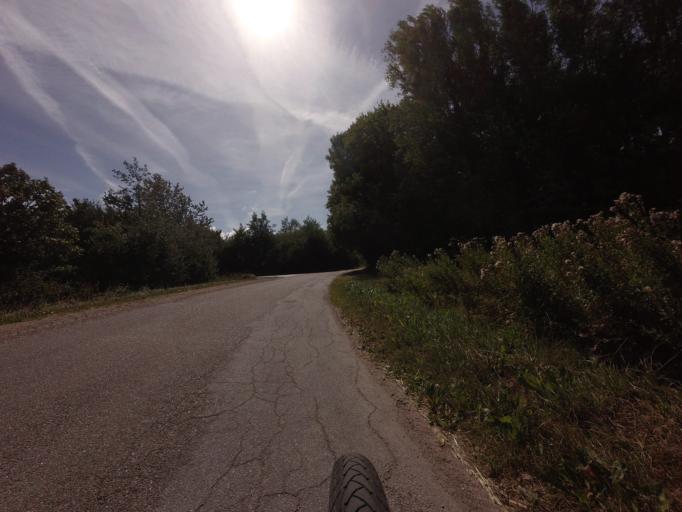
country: DK
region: North Denmark
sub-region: Hjorring Kommune
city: Vra
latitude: 57.3394
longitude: 9.8090
